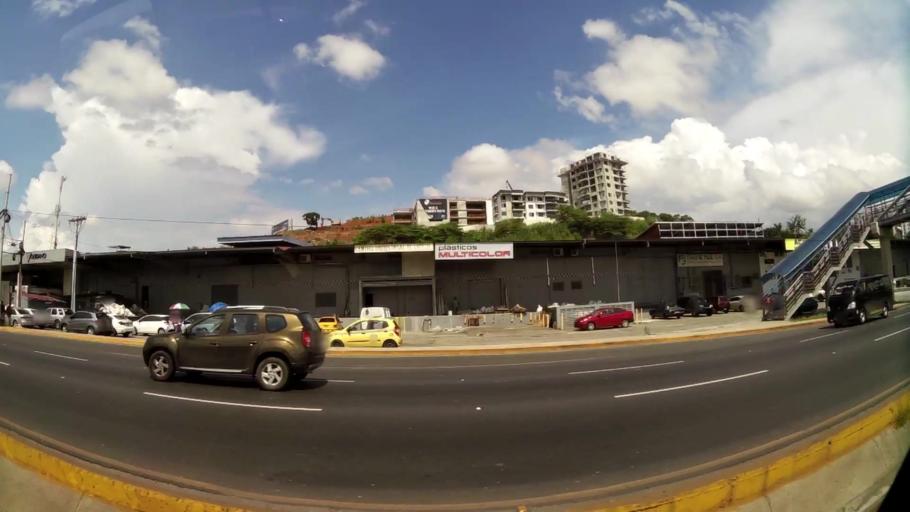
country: PA
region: Panama
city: San Miguelito
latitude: 9.0451
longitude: -79.4695
